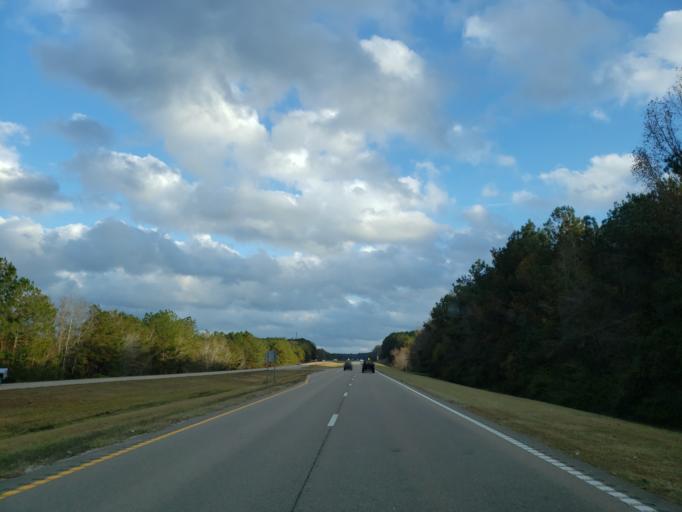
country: US
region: Mississippi
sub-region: Perry County
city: New Augusta
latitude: 31.1647
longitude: -88.9329
